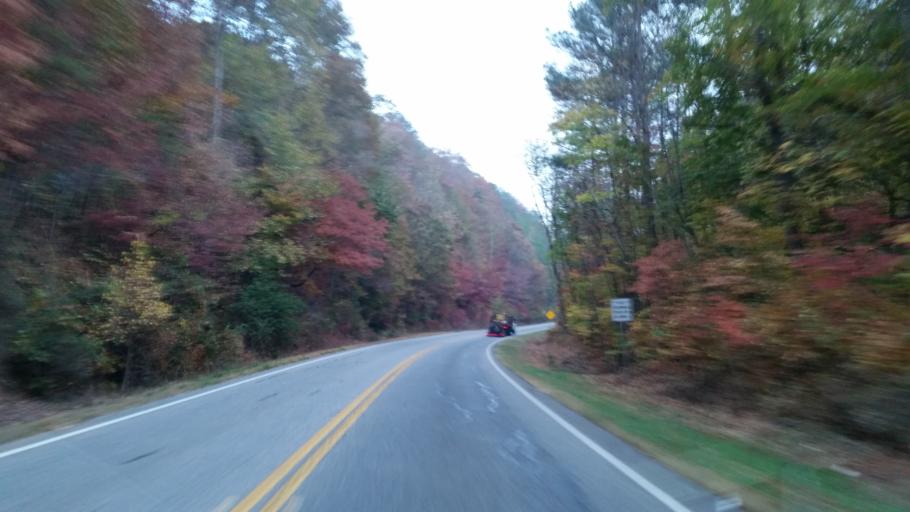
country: US
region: Georgia
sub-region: Gilmer County
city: Ellijay
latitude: 34.5815
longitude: -84.6514
